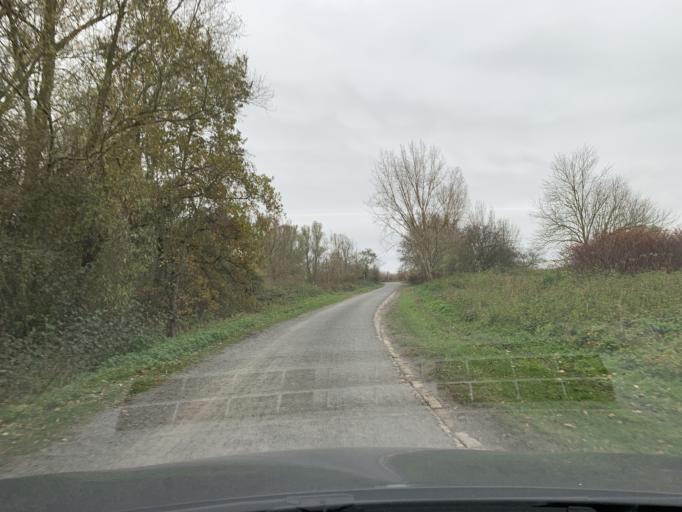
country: FR
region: Nord-Pas-de-Calais
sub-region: Departement du Pas-de-Calais
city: Ecourt-Saint-Quentin
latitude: 50.2507
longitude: 3.0980
